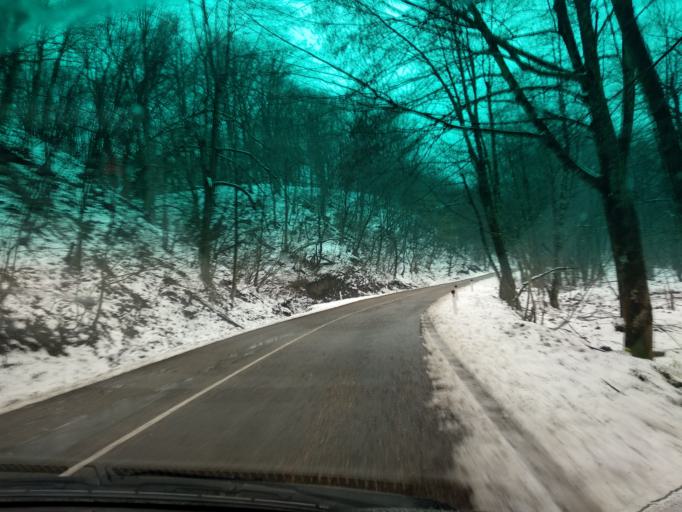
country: RU
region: Krasnodarskiy
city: Khadyzhensk
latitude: 44.2092
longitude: 39.4250
